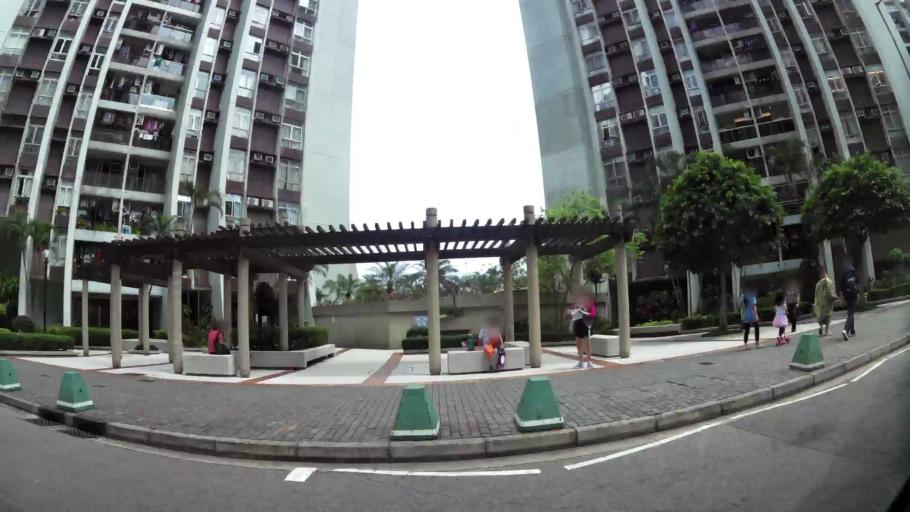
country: HK
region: Wanchai
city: Wan Chai
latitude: 22.2870
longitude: 114.2151
